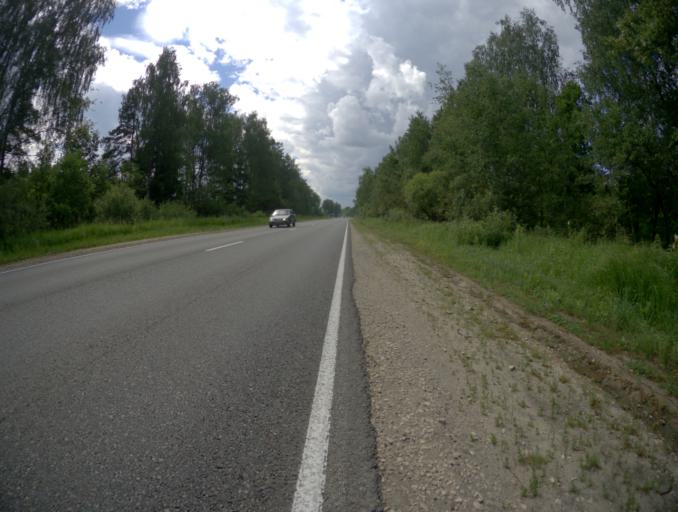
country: RU
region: Vladimir
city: Golovino
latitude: 56.0016
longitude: 40.5659
